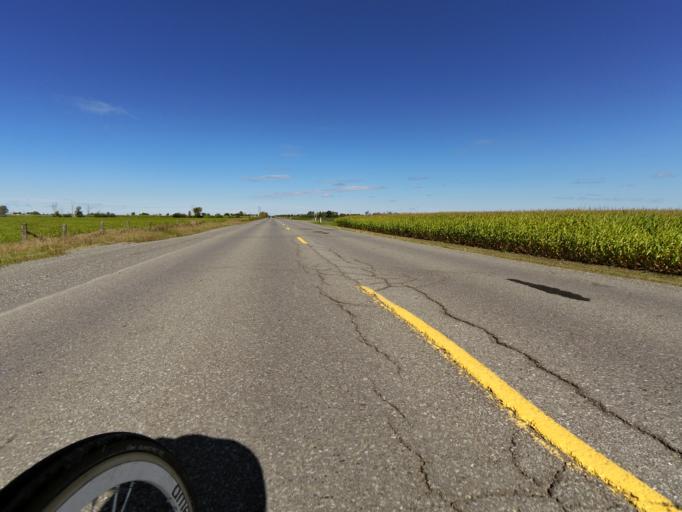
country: CA
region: Ontario
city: Bells Corners
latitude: 45.2214
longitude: -75.8318
